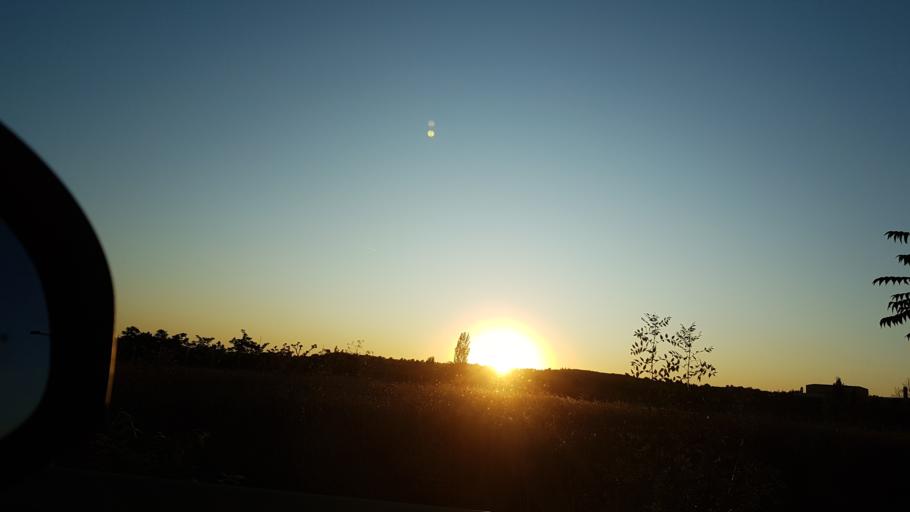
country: TR
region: Ankara
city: Batikent
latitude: 39.9237
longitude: 32.7059
